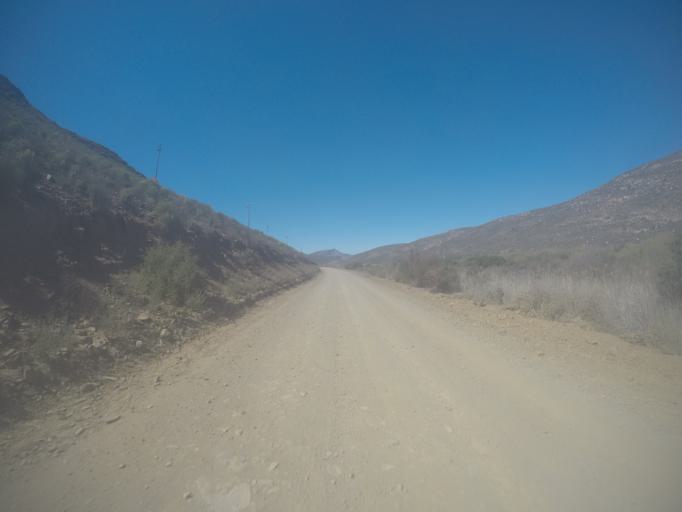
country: ZA
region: Western Cape
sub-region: West Coast District Municipality
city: Clanwilliam
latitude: -32.5097
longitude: 19.3432
